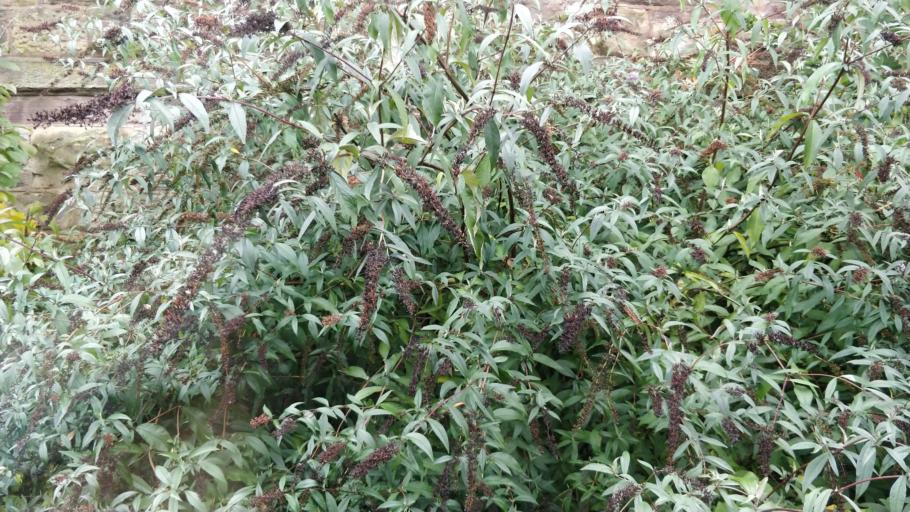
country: GB
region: England
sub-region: Borough of Wigan
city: Ince-in-Makerfield
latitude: 53.5453
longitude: -2.6343
